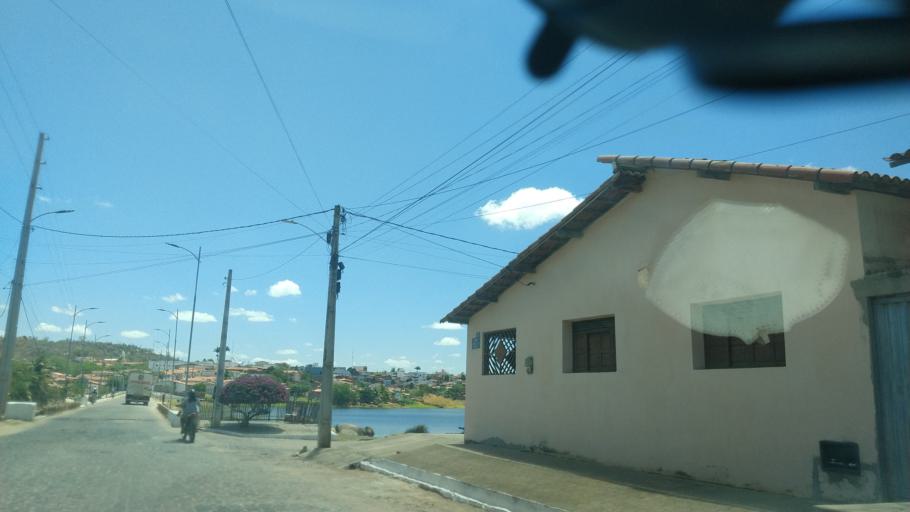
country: BR
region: Rio Grande do Norte
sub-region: Cerro Cora
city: Cerro Cora
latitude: -6.0396
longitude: -36.3467
